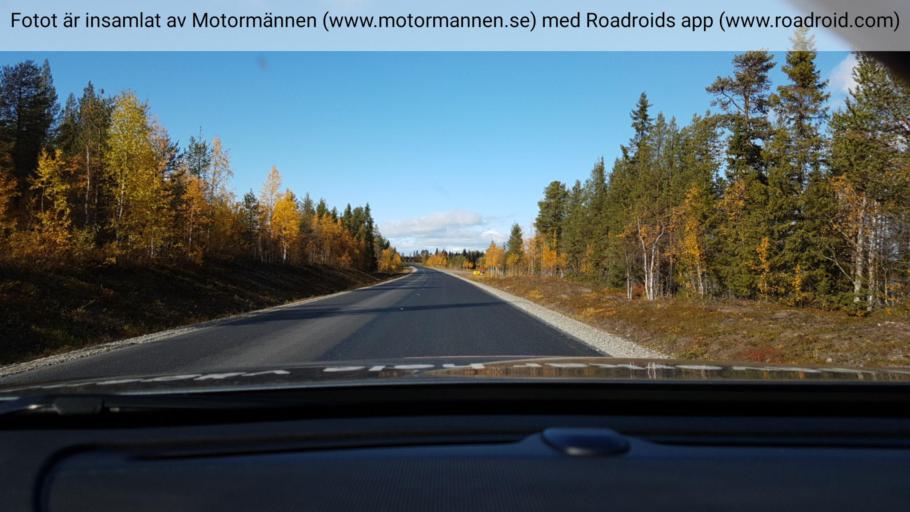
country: SE
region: Norrbotten
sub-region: Arjeplogs Kommun
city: Arjeplog
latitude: 65.9747
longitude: 18.2401
